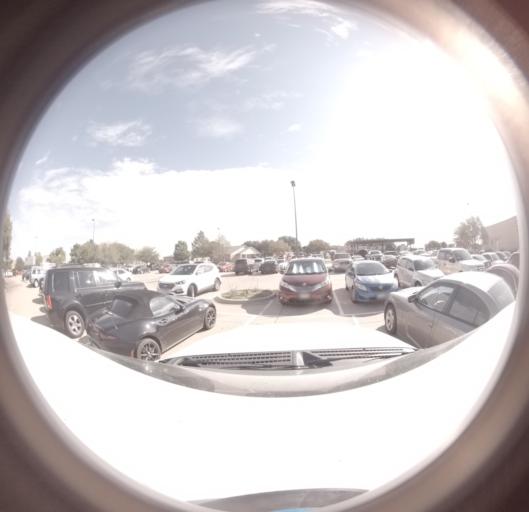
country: US
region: Texas
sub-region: Ector County
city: West Odessa
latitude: 31.7427
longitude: -102.5296
